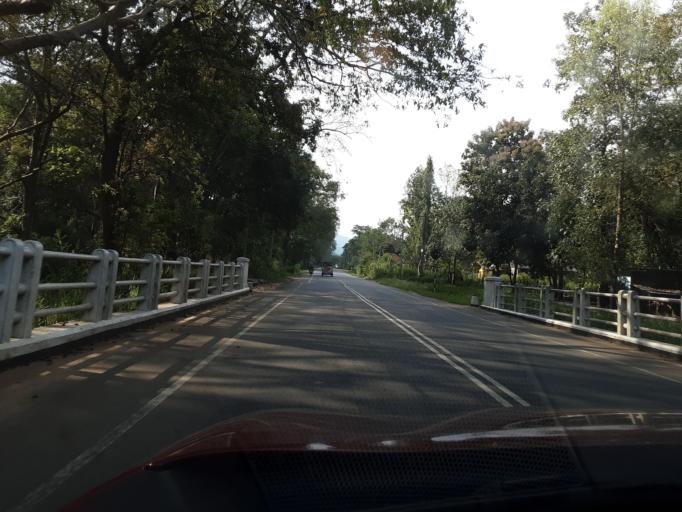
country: LK
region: Uva
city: Haputale
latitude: 6.6803
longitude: 81.1102
